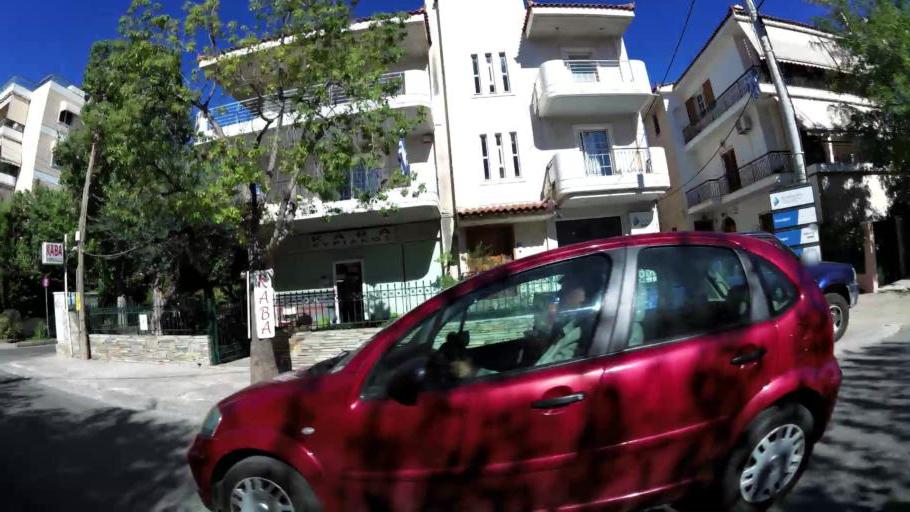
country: GR
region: Attica
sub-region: Nomarchia Athinas
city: Vrilissia
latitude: 38.0267
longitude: 23.8214
